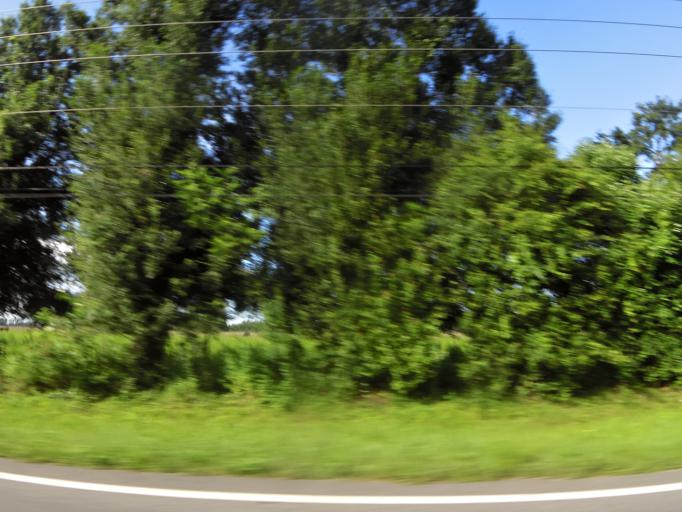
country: US
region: Florida
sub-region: Clay County
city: Green Cove Springs
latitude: 29.9868
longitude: -81.5278
